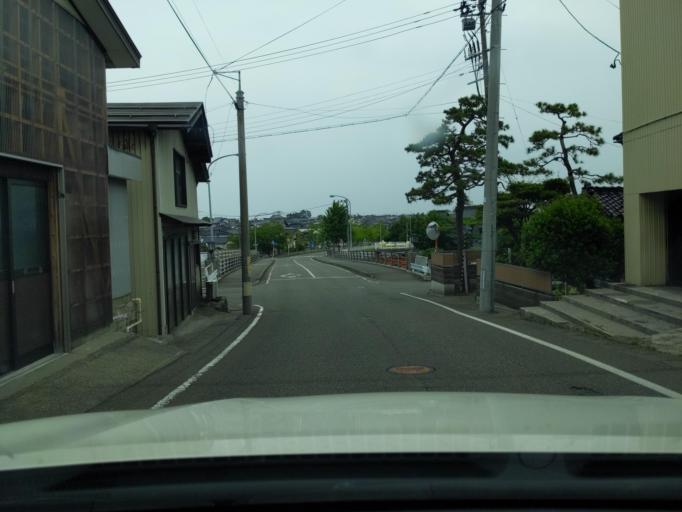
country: JP
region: Niigata
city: Kashiwazaki
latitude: 37.3638
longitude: 138.5460
